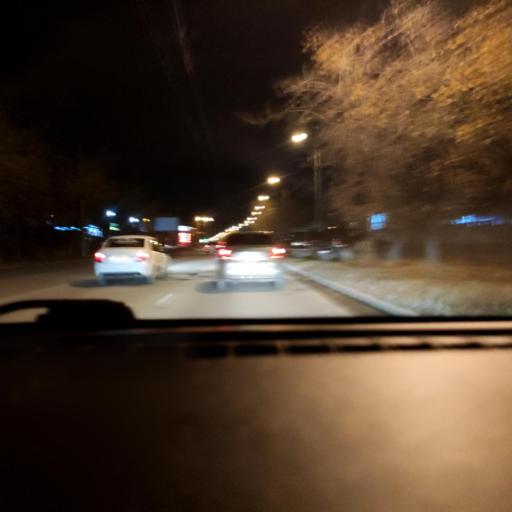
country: RU
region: Perm
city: Perm
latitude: 57.9707
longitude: 56.2459
